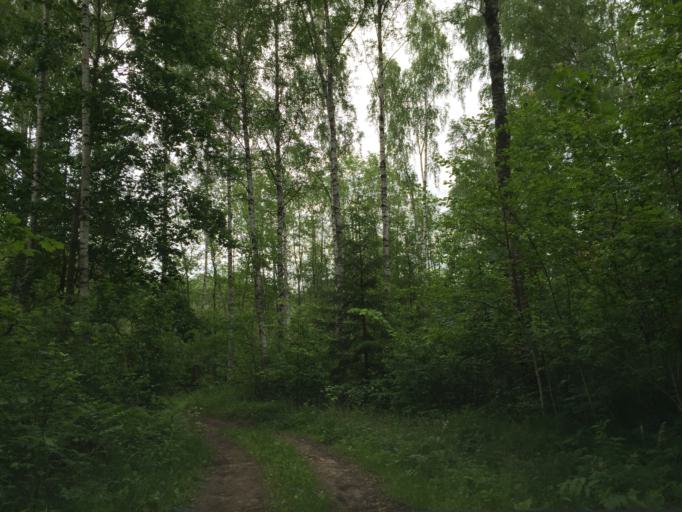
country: LV
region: Apes Novads
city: Ape
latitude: 57.4230
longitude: 26.3661
